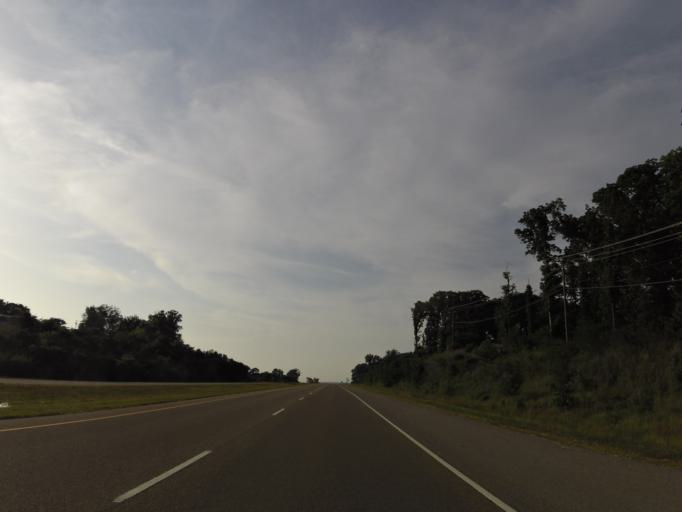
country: US
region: Tennessee
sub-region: Loudon County
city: Lenoir City
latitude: 35.7662
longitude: -84.2295
